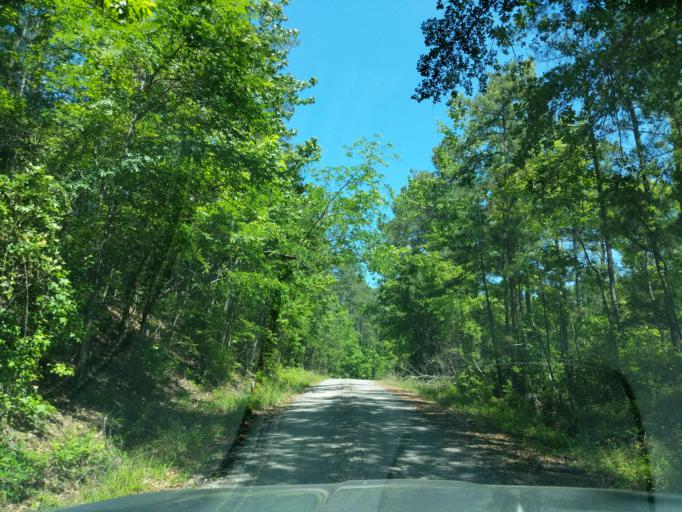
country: US
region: Georgia
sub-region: Columbia County
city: Evans
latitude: 33.6194
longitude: -82.1156
